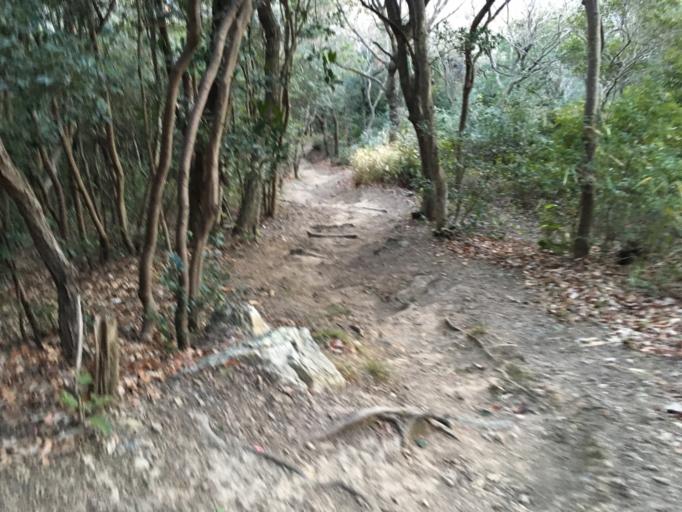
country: JP
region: Aichi
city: Toyohashi
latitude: 34.7301
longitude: 137.4433
